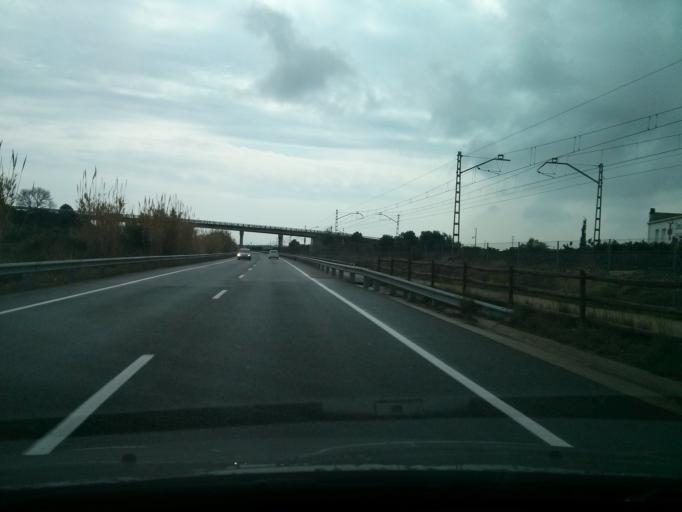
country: ES
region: Catalonia
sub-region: Provincia de Tarragona
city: El Vendrell
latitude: 41.2101
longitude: 1.5350
